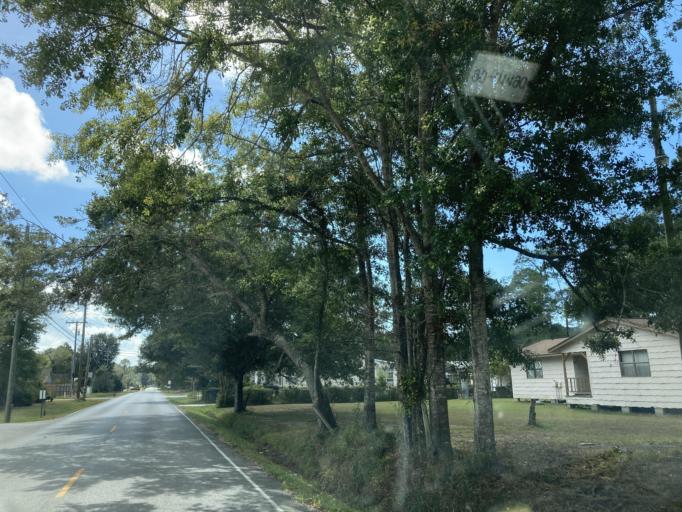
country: US
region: Mississippi
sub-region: Jackson County
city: Gulf Hills
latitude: 30.4484
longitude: -88.8304
